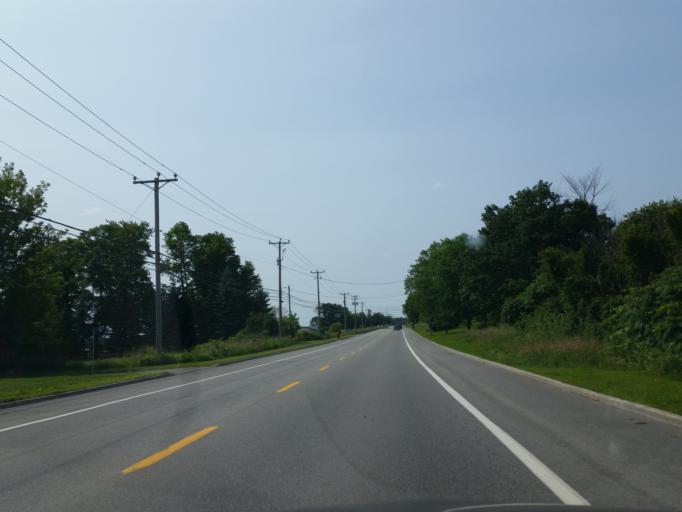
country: CA
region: Ontario
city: Bells Corners
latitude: 45.4232
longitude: -75.8917
